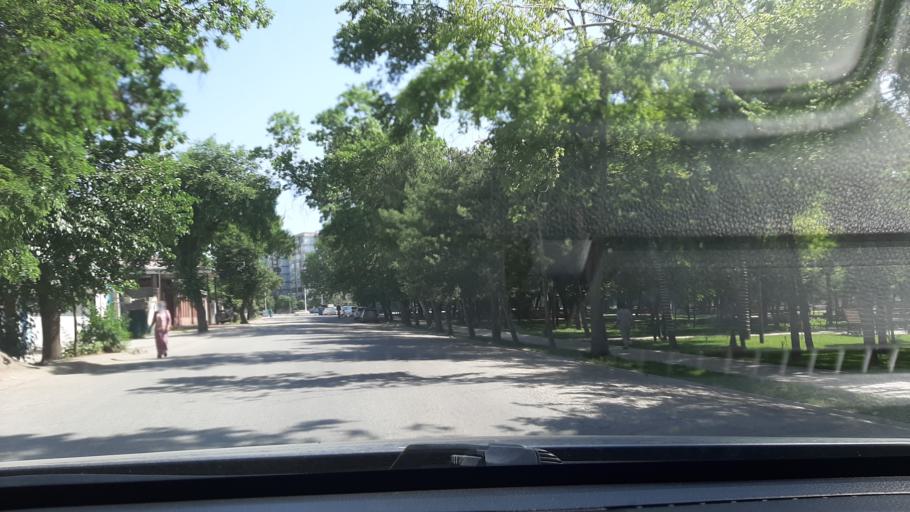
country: TJ
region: Dushanbe
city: Dushanbe
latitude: 38.5568
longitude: 68.7571
